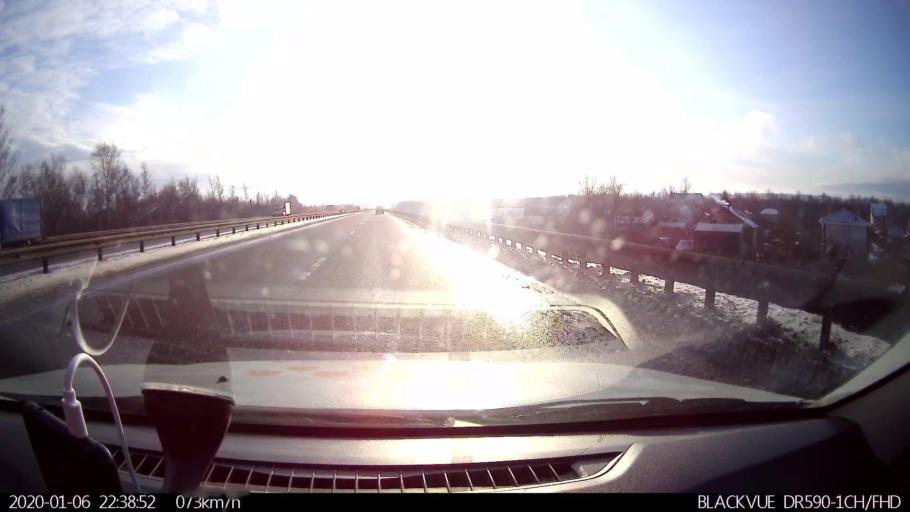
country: RU
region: Nizjnij Novgorod
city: Gorbatovka
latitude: 56.2157
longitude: 43.7501
